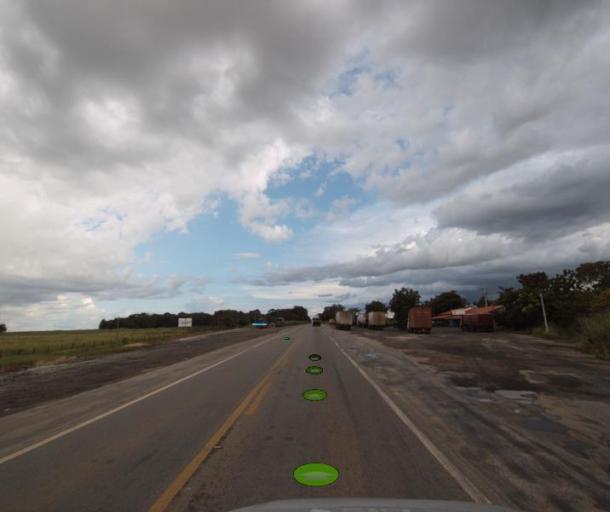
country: BR
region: Goias
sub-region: Porangatu
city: Porangatu
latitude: -13.3496
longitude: -49.1227
